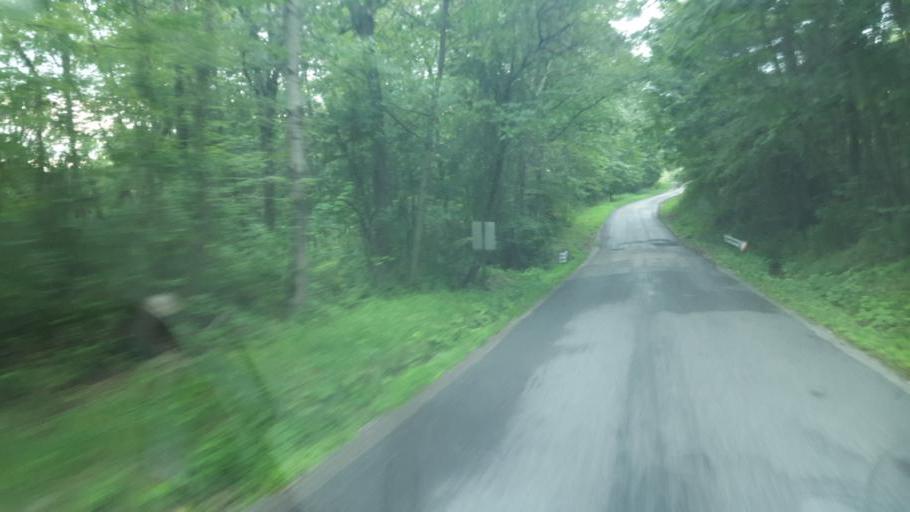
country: US
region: Pennsylvania
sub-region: Clarion County
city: Clarion
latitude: 41.1765
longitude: -79.3798
